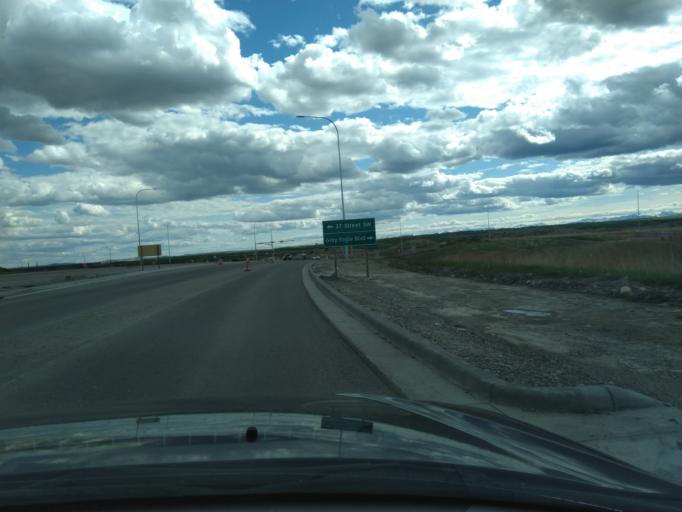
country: CA
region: Alberta
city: Calgary
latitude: 51.0053
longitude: -114.1422
